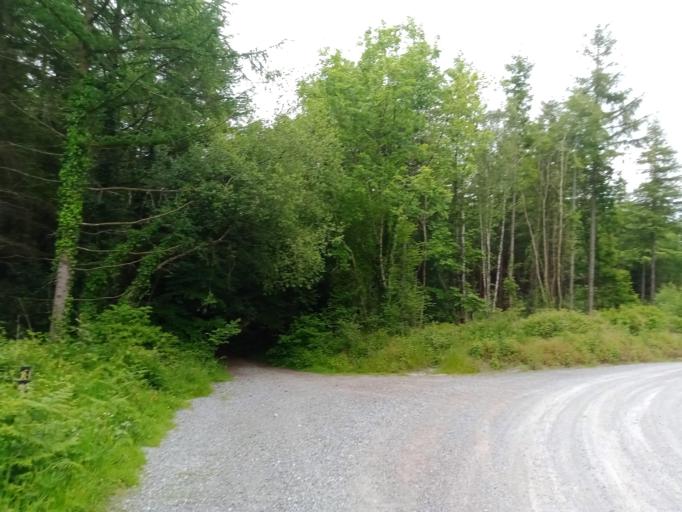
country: IE
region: Leinster
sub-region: Kilkenny
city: Thomastown
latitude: 52.4701
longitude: -7.0506
